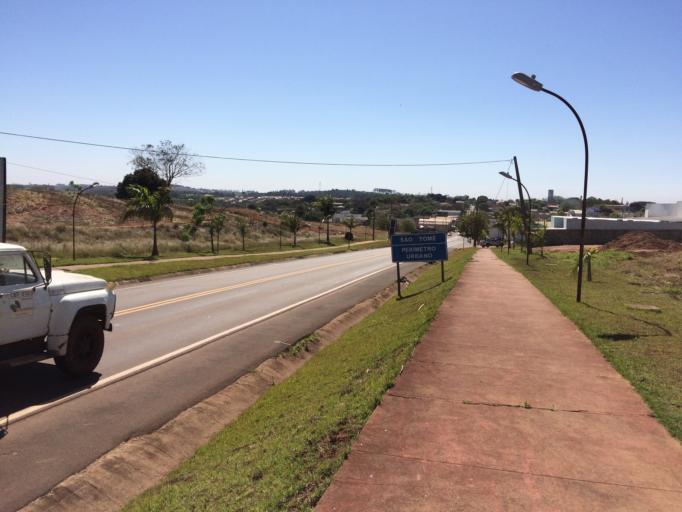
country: BR
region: Parana
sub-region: Cianorte
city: Cianorte
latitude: -23.5388
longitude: -52.5986
